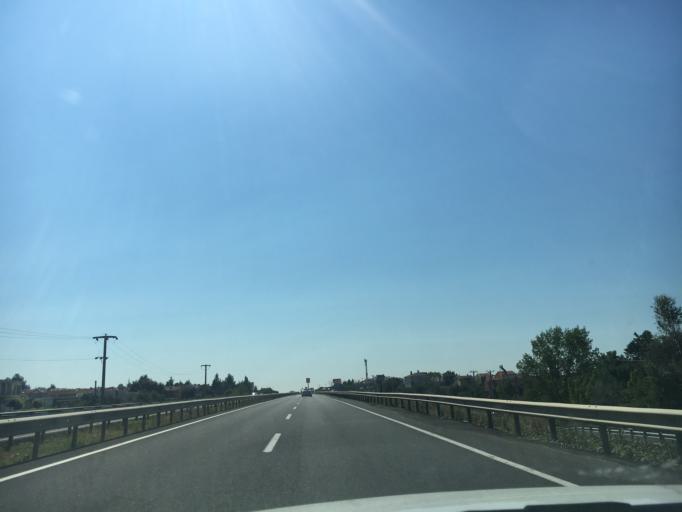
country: TR
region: Tekirdag
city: Marmara Ereglisi
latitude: 40.9749
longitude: 27.8765
